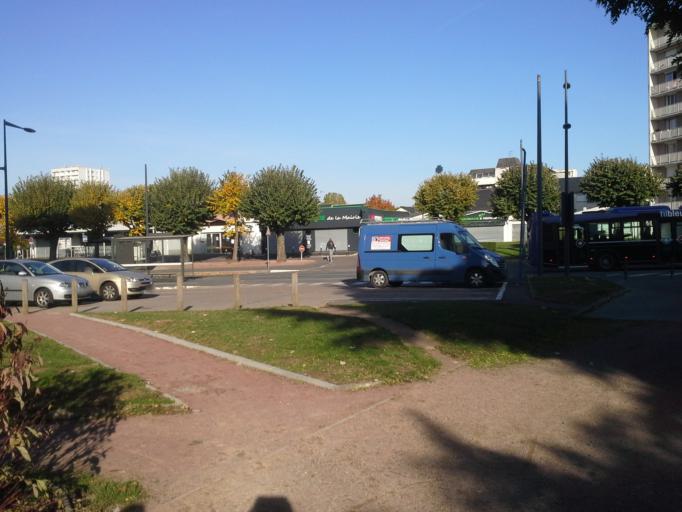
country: FR
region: Centre
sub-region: Departement d'Indre-et-Loire
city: La Riche
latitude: 47.3874
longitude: 0.6584
